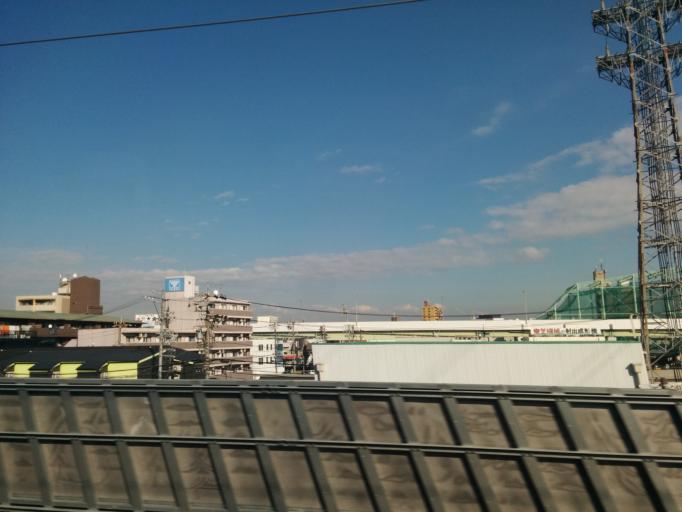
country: JP
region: Aichi
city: Nagoya-shi
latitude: 35.0969
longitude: 136.9259
